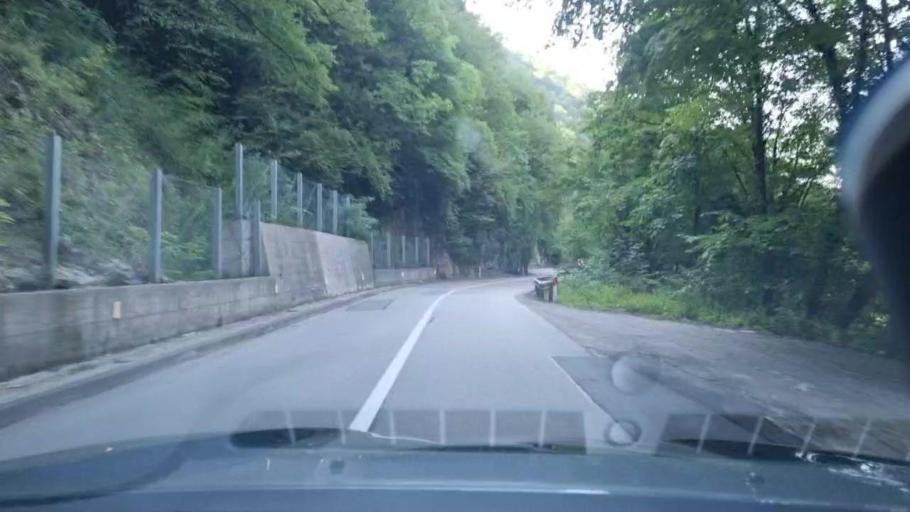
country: BA
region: Federation of Bosnia and Herzegovina
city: Stijena
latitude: 44.8906
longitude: 16.0519
